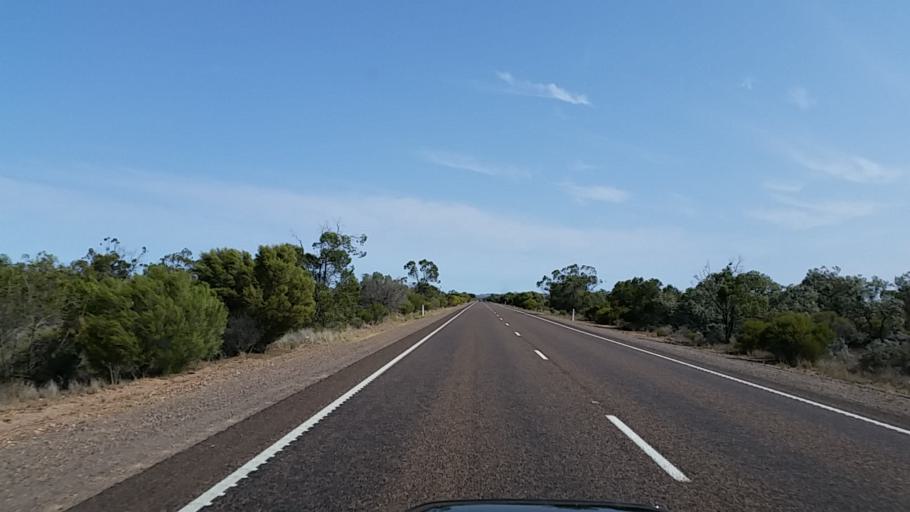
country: AU
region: South Australia
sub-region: Port Augusta
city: Port Augusta West
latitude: -32.6723
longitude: 137.5256
